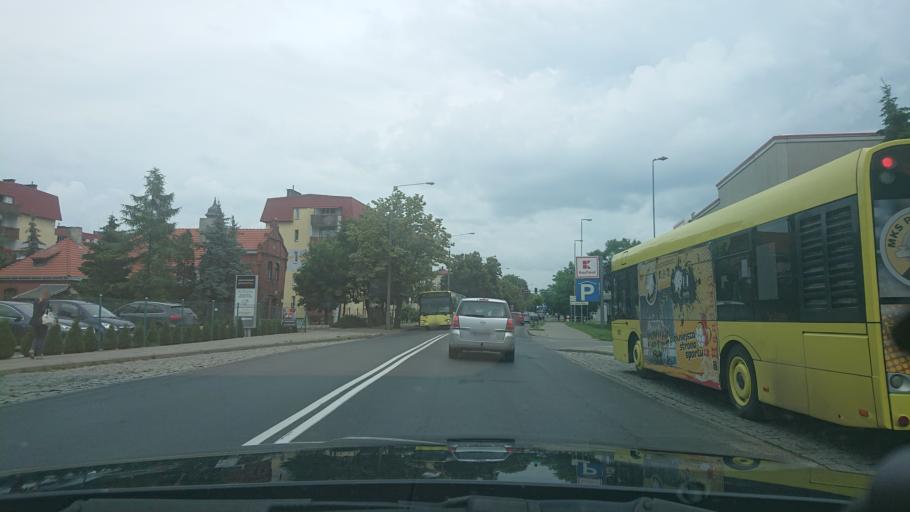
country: PL
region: Greater Poland Voivodeship
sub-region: Powiat gnieznienski
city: Gniezno
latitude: 52.5386
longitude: 17.6099
